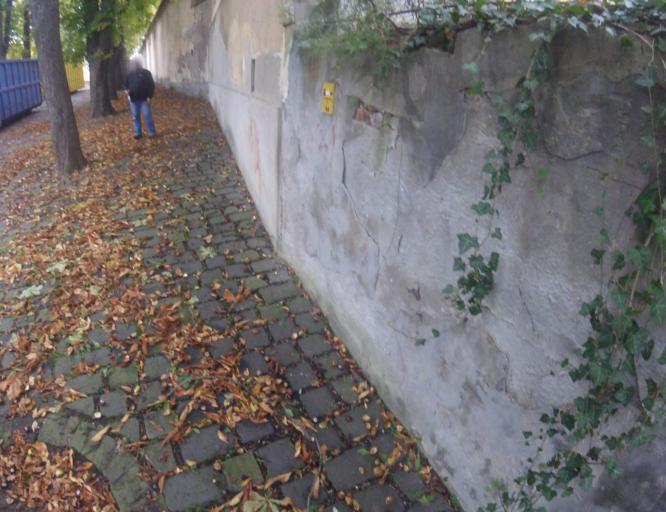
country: HU
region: Pest
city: Szob
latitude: 47.8155
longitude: 18.8659
